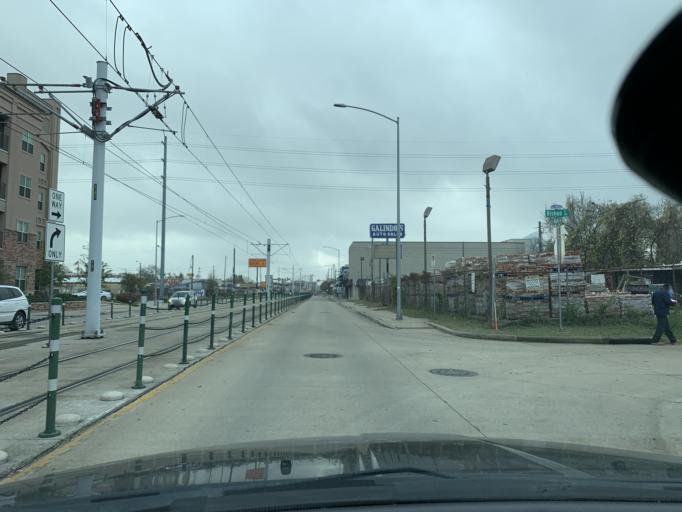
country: US
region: Texas
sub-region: Harris County
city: Houston
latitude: 29.7780
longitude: -95.3626
